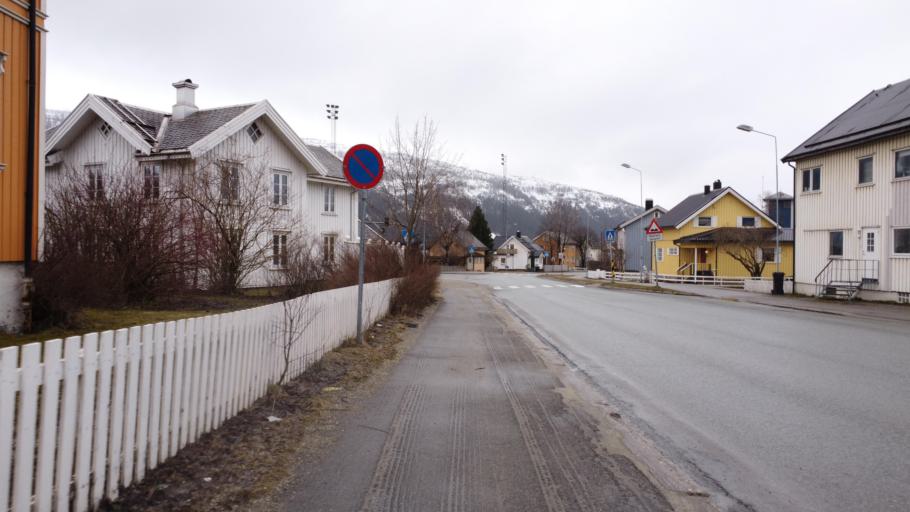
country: NO
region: Nordland
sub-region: Rana
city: Mo i Rana
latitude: 66.3134
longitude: 14.1521
